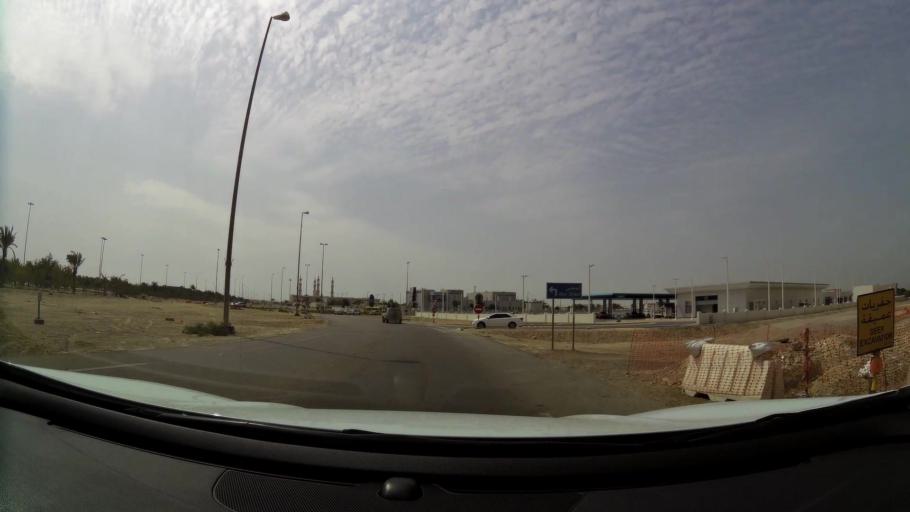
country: AE
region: Abu Dhabi
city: Abu Dhabi
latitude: 24.5215
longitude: 54.6707
